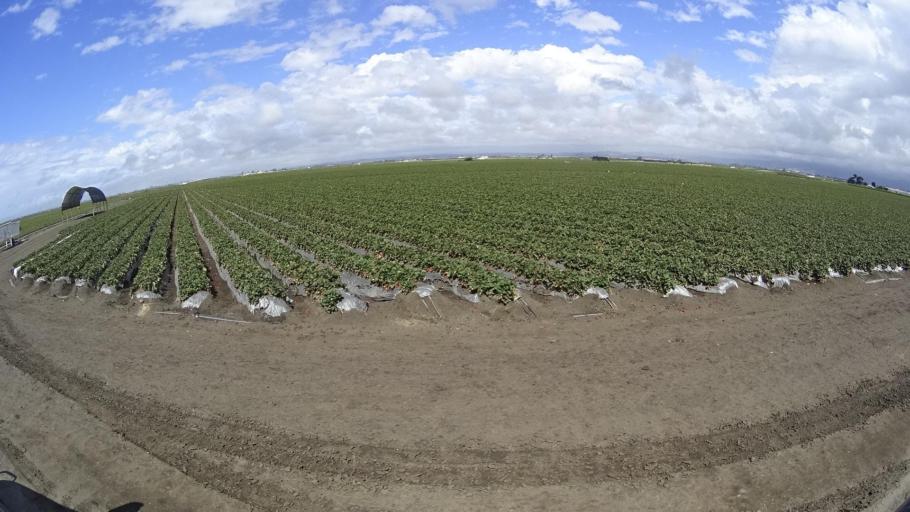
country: US
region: California
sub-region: Monterey County
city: Boronda
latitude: 36.6941
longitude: -121.7182
